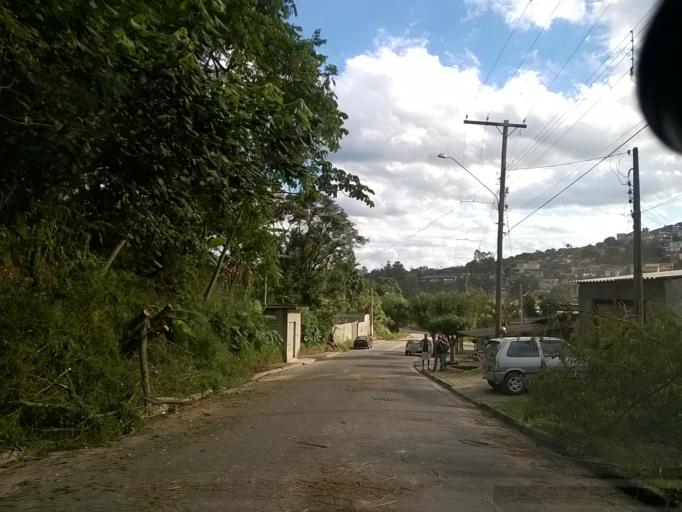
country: BR
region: Sao Paulo
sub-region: Francisco Morato
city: Francisco Morato
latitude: -23.2900
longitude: -46.7521
